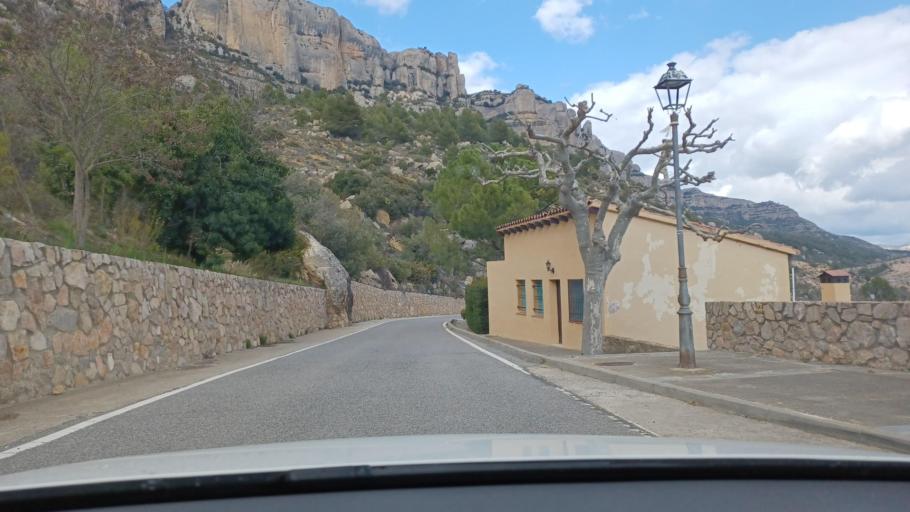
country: ES
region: Catalonia
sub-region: Provincia de Tarragona
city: la Morera de Montsant
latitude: 41.2667
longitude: 0.8428
